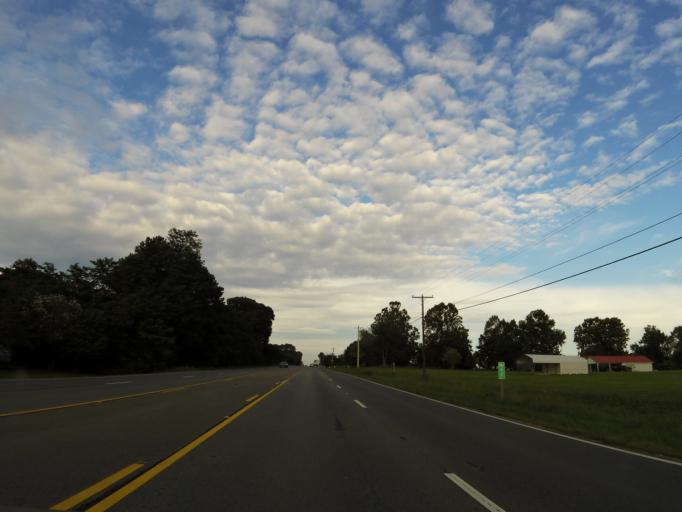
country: US
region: Alabama
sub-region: Lauderdale County
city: Rogersville
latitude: 34.8012
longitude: -87.2137
